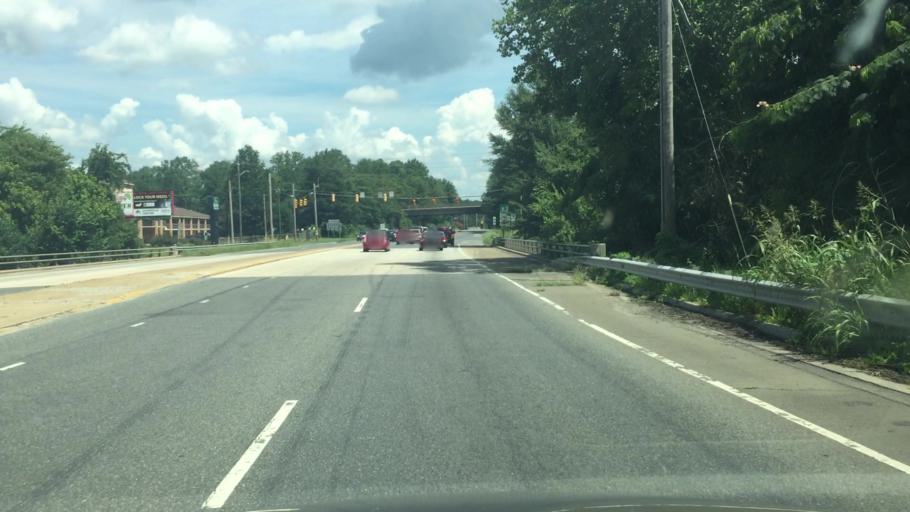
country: US
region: North Carolina
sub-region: Richmond County
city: Rockingham
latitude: 34.9367
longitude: -79.7798
